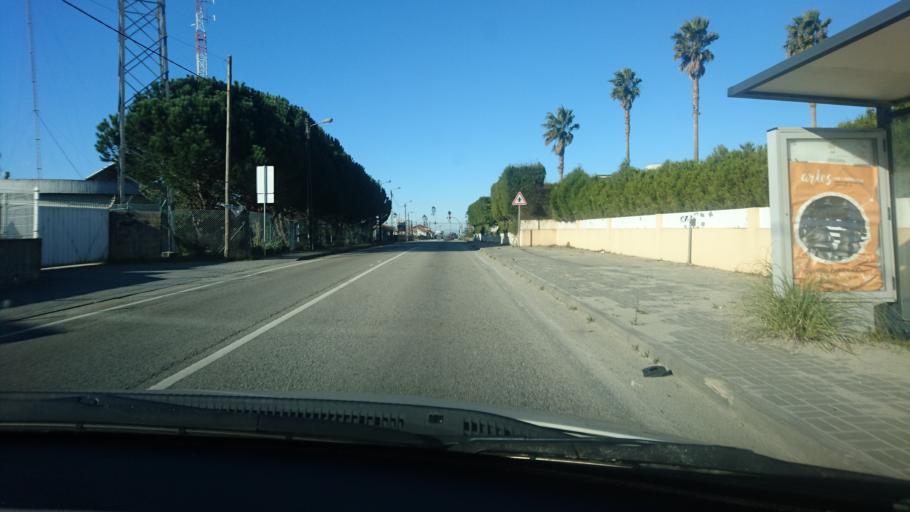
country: PT
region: Aveiro
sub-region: Santa Maria da Feira
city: Sao Joao de Ver
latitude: 40.9516
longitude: -8.5177
